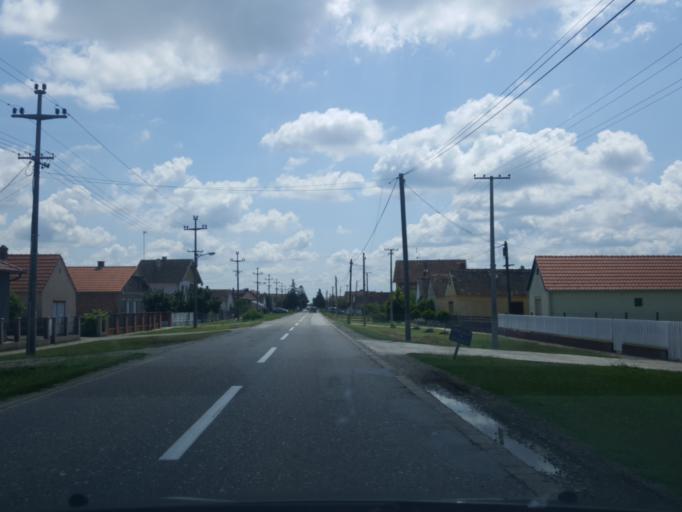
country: RS
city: Glusci
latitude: 44.8880
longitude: 19.5503
